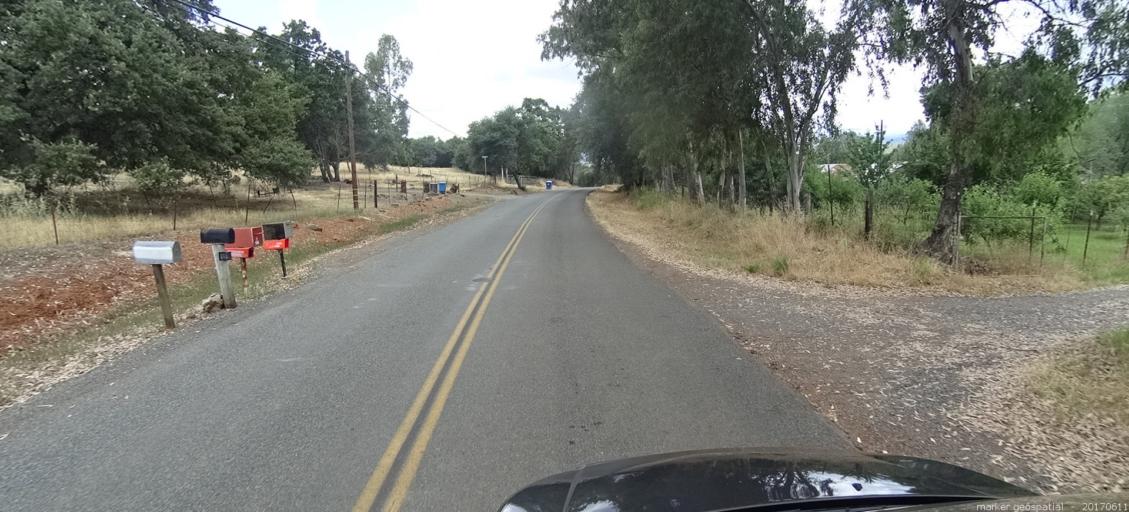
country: US
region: California
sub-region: Butte County
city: Oroville
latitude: 39.6336
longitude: -121.5284
